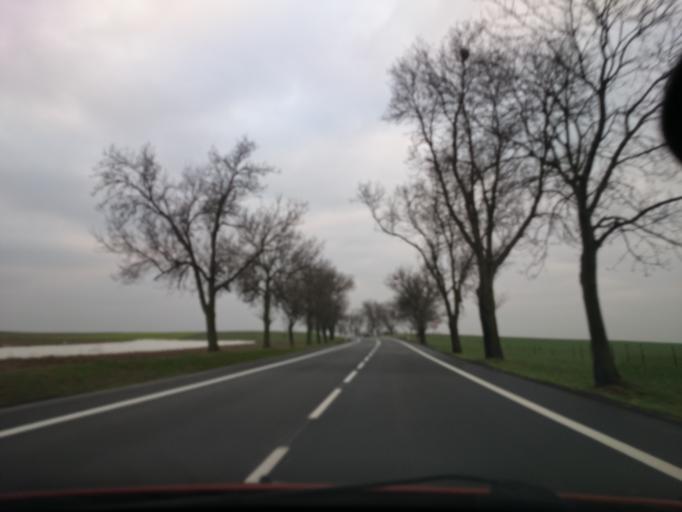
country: PL
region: Opole Voivodeship
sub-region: Powiat nyski
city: Sidzina
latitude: 50.5647
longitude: 17.4361
